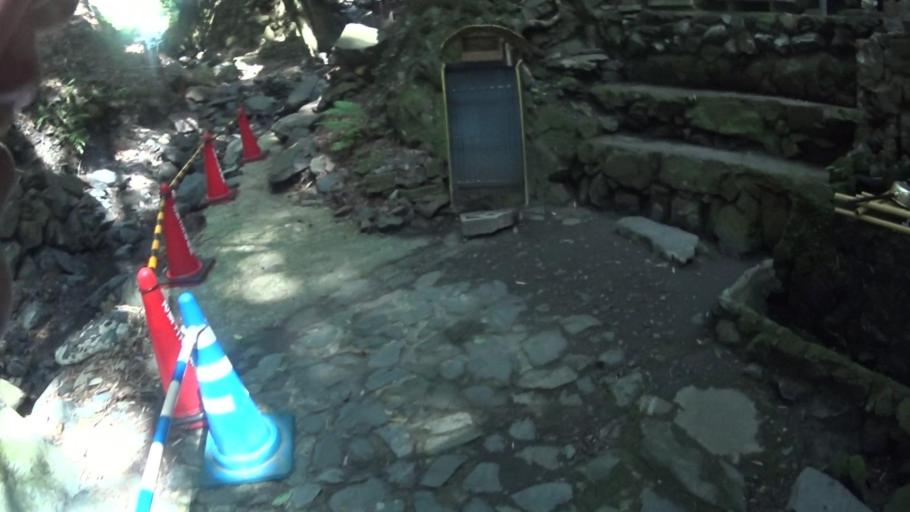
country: JP
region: Kyoto
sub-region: Kyoto-shi
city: Kamigyo-ku
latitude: 35.0165
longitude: 135.7999
